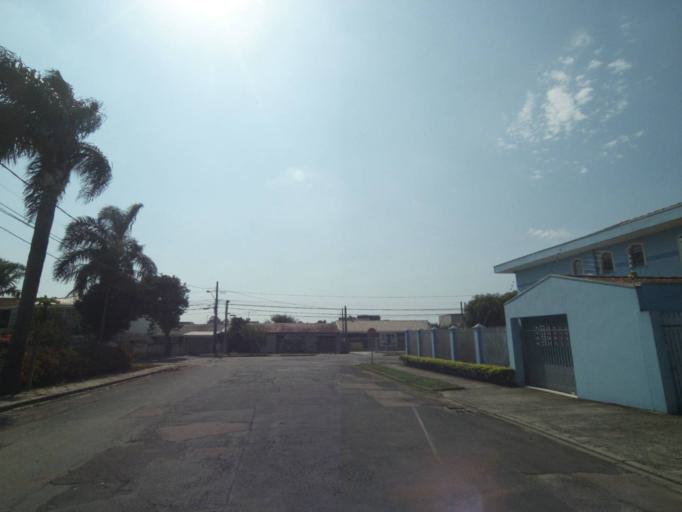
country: BR
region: Parana
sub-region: Curitiba
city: Curitiba
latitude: -25.4855
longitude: -49.3312
